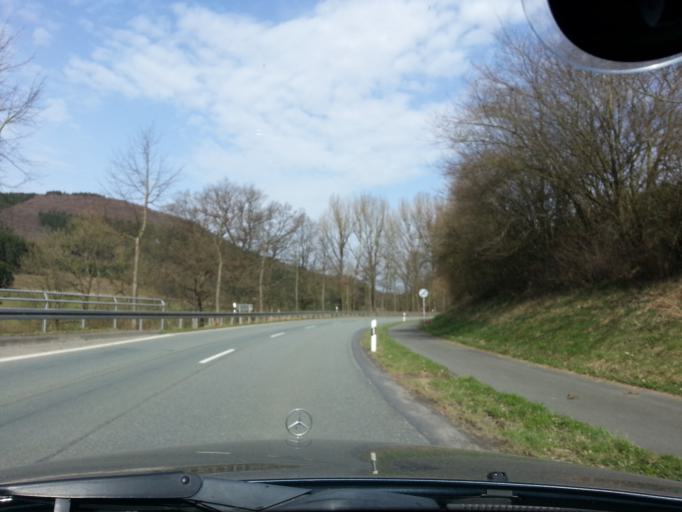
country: DE
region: North Rhine-Westphalia
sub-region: Regierungsbezirk Arnsberg
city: Meschede
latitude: 51.2850
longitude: 8.3327
